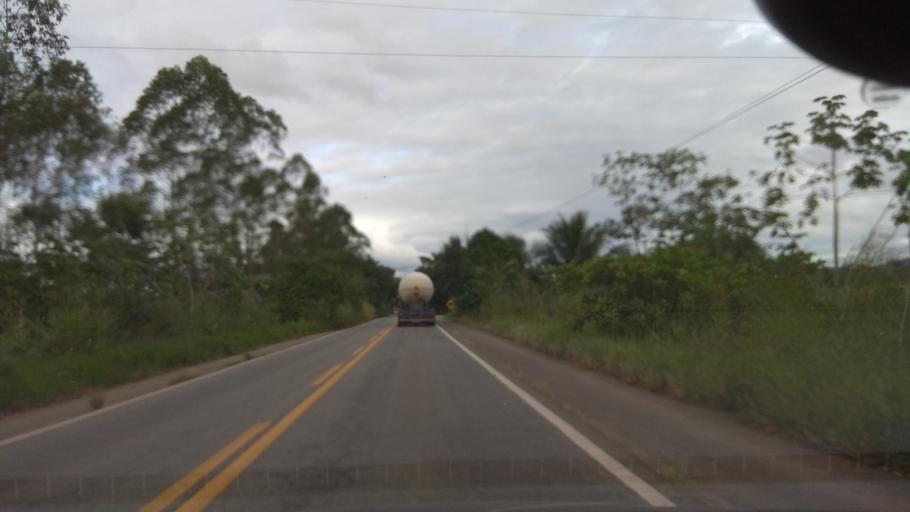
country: BR
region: Bahia
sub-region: Ipiau
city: Ipiau
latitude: -14.1635
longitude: -39.6897
